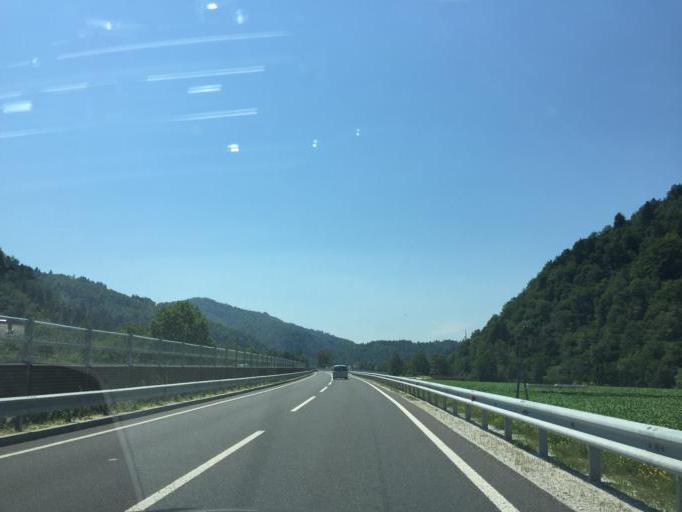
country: SI
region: Skofja Loka
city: Skofja Loka
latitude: 46.1526
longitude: 14.2936
